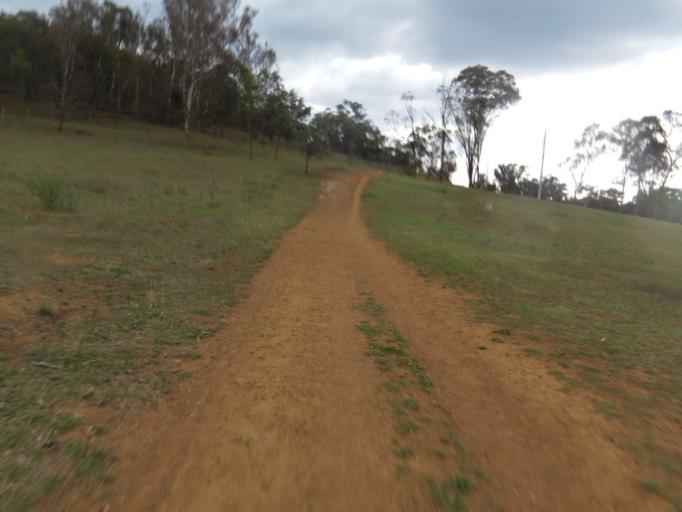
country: AU
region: Australian Capital Territory
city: Forrest
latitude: -35.3330
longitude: 149.1204
